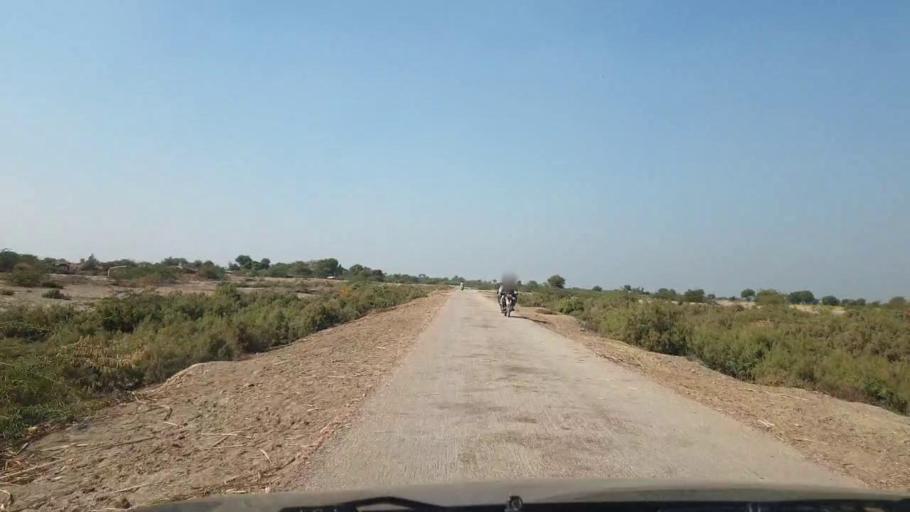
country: PK
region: Sindh
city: Jhol
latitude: 25.9083
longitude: 68.8287
